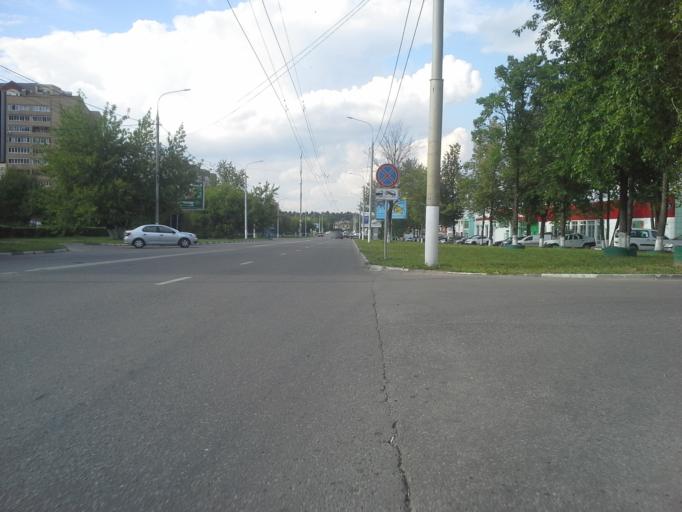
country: RU
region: Moskovskaya
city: Dubrovitsy
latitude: 55.4304
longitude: 37.5070
